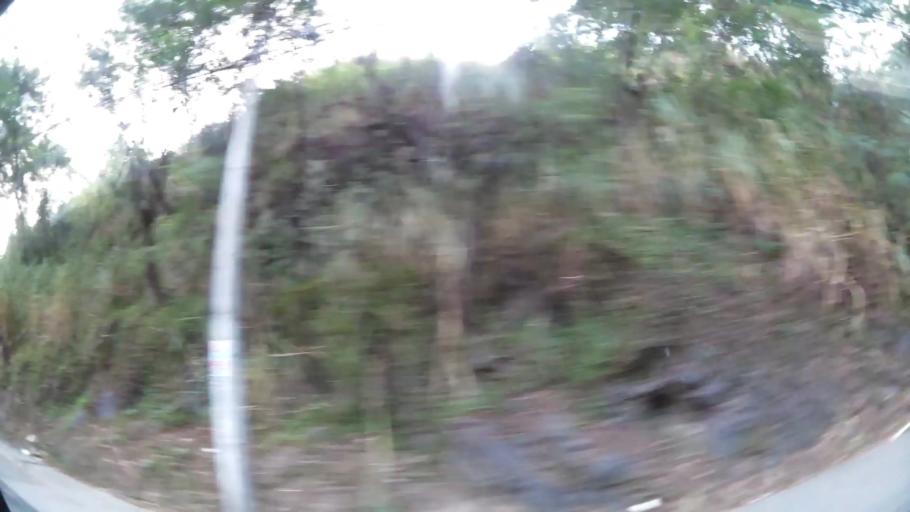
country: CO
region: Antioquia
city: Medellin
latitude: 6.2280
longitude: -75.5687
